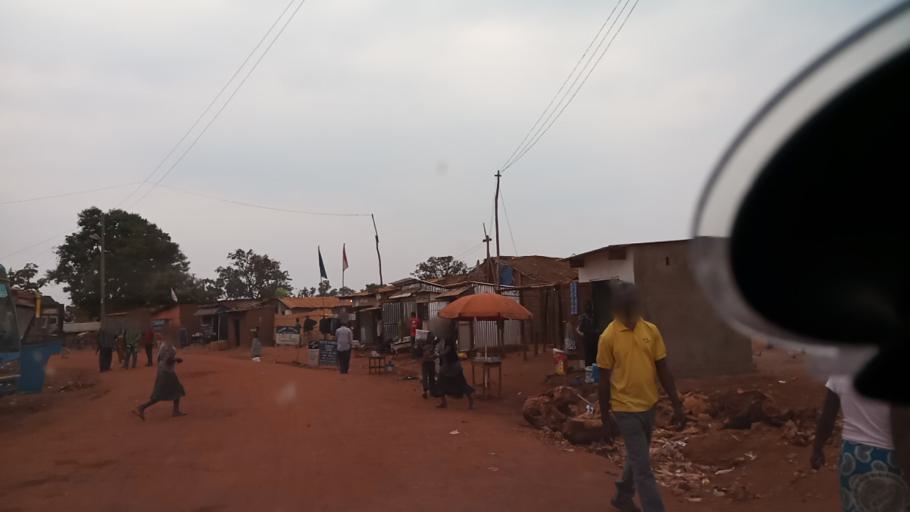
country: ZM
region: Luapula
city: Nchelenge
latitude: -9.2785
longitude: 28.3342
